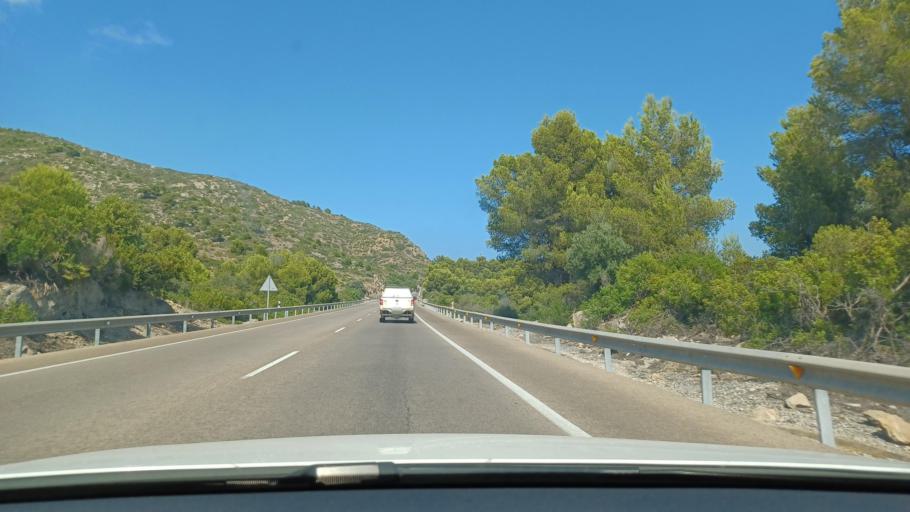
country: ES
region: Valencia
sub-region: Provincia de Castello
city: Benicassim
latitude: 40.0694
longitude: 0.0980
